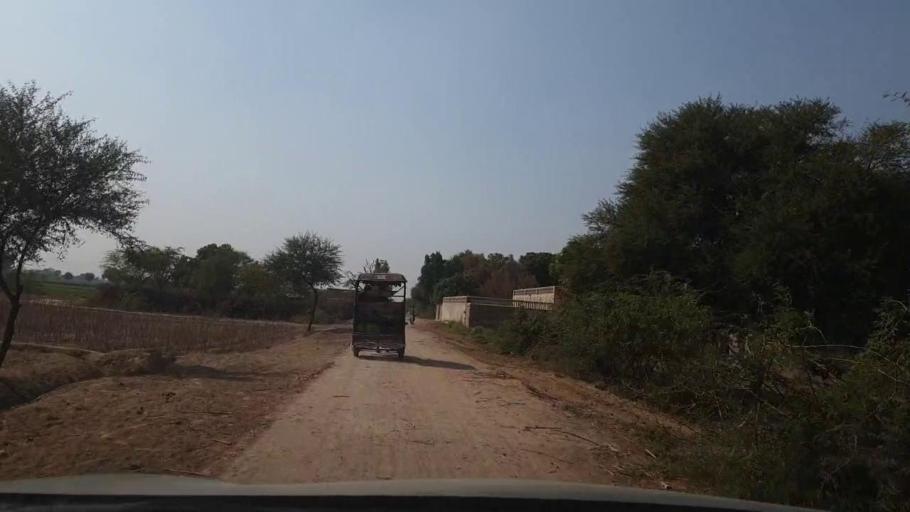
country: PK
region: Sindh
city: Tando Allahyar
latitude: 25.5570
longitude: 68.8343
